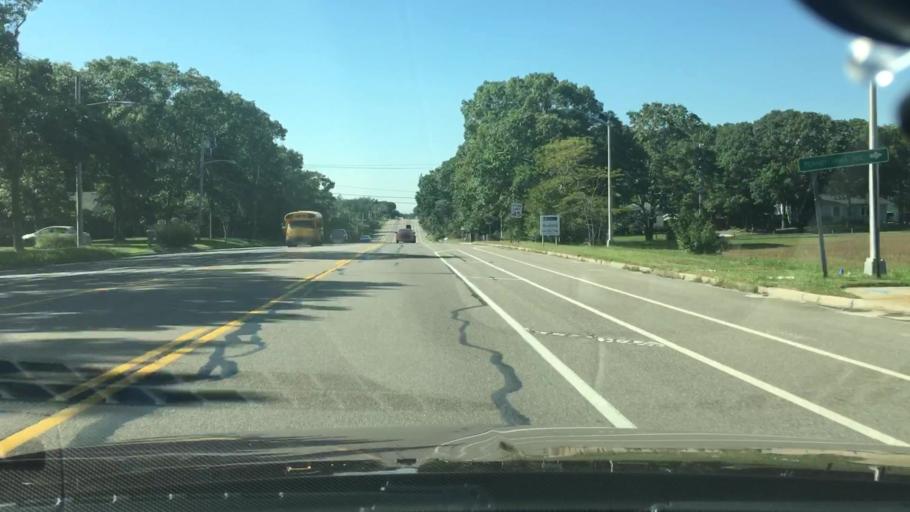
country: US
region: New York
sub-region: Suffolk County
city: North Patchogue
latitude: 40.7954
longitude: -72.9911
